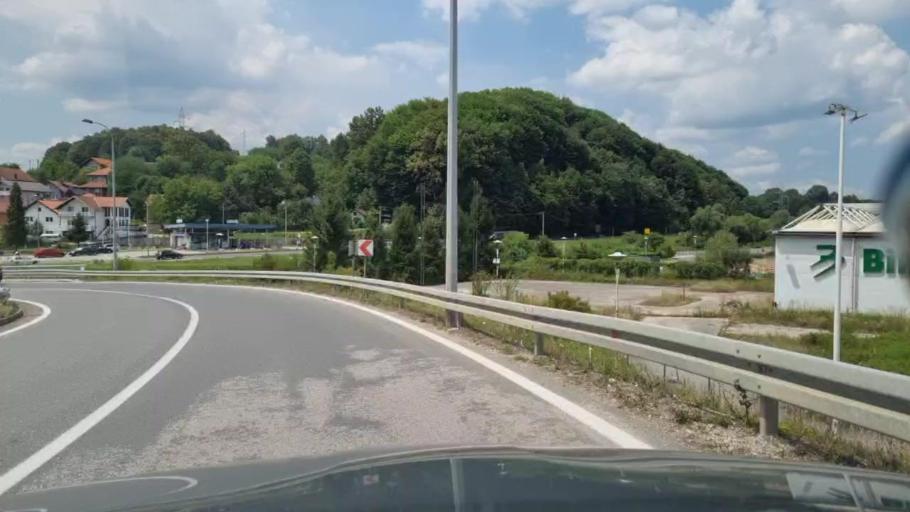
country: BA
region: Federation of Bosnia and Herzegovina
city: Kiseljak
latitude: 44.5199
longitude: 18.5881
